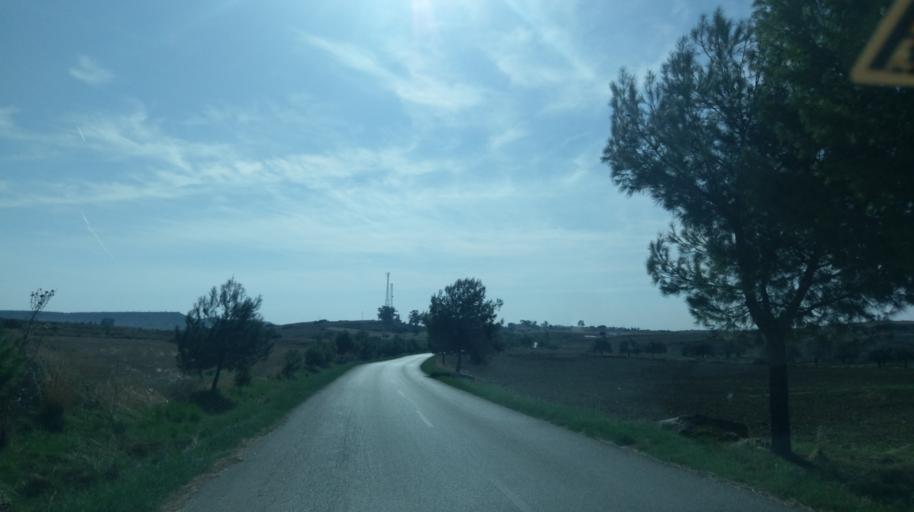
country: CY
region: Ammochostos
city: Trikomo
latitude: 35.3780
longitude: 34.0011
